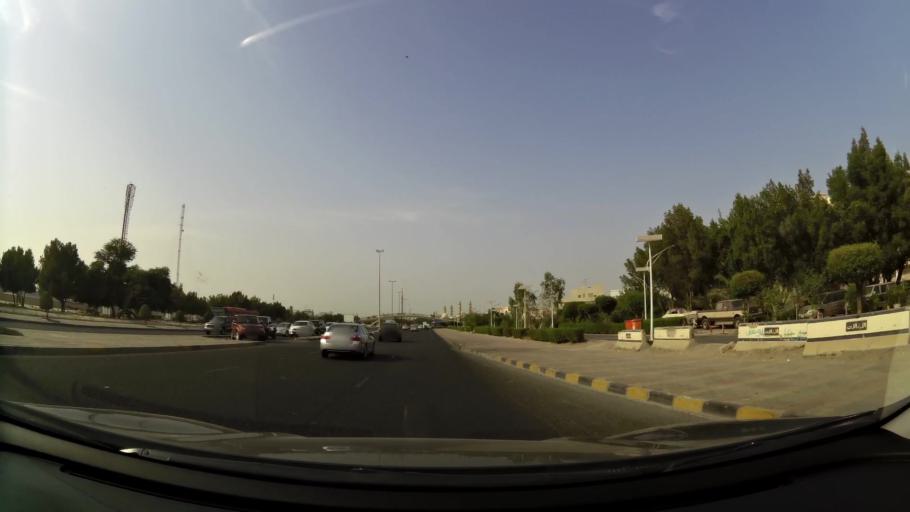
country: KW
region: Al Asimah
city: Ash Shamiyah
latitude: 29.3271
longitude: 47.9563
